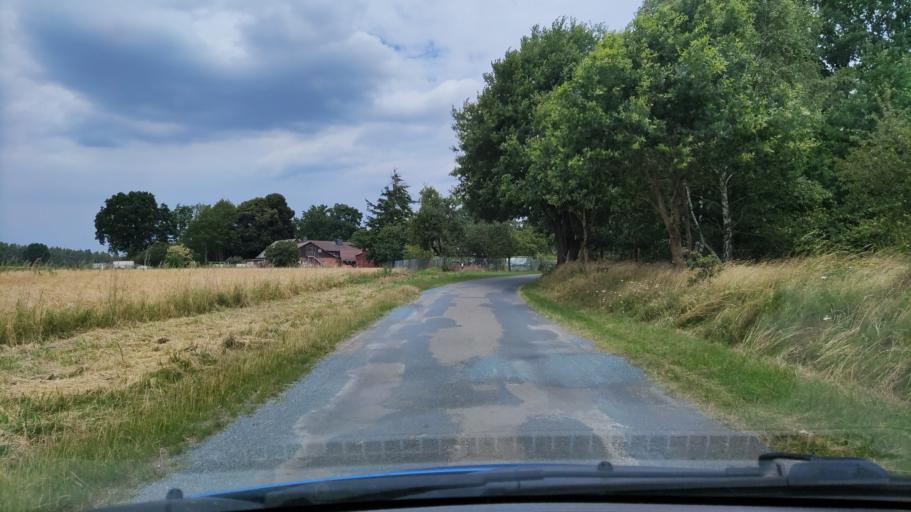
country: DE
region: Lower Saxony
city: Schnega
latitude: 52.9382
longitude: 10.8794
